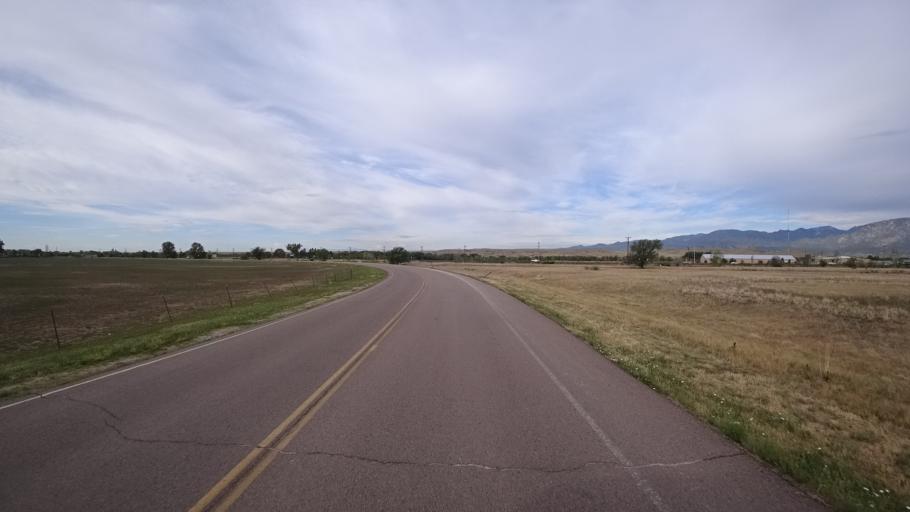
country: US
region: Colorado
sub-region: El Paso County
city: Security-Widefield
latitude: 38.7201
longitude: -104.7135
